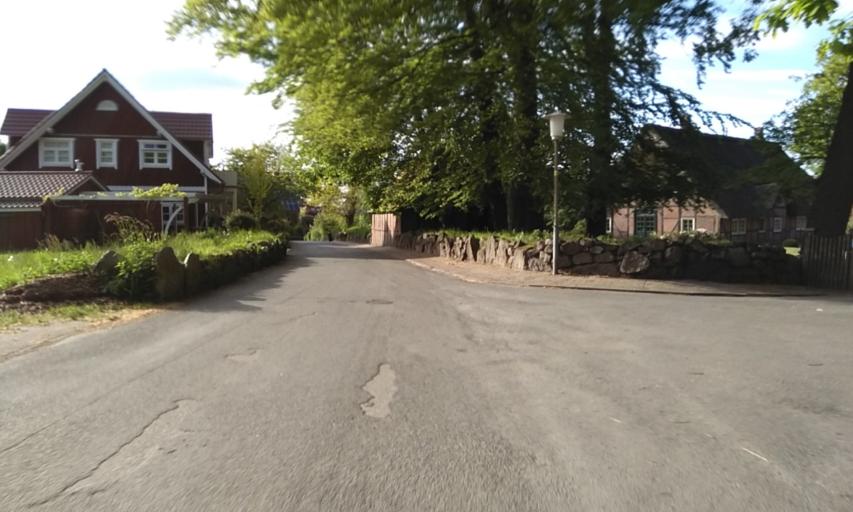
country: DE
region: Lower Saxony
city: Nottensdorf
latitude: 53.4829
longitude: 9.6029
